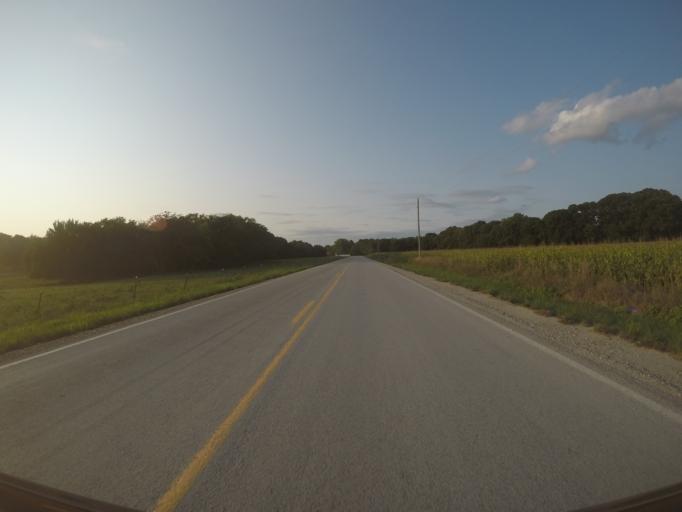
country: US
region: Kansas
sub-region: Pottawatomie County
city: Wamego
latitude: 39.1344
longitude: -96.4267
